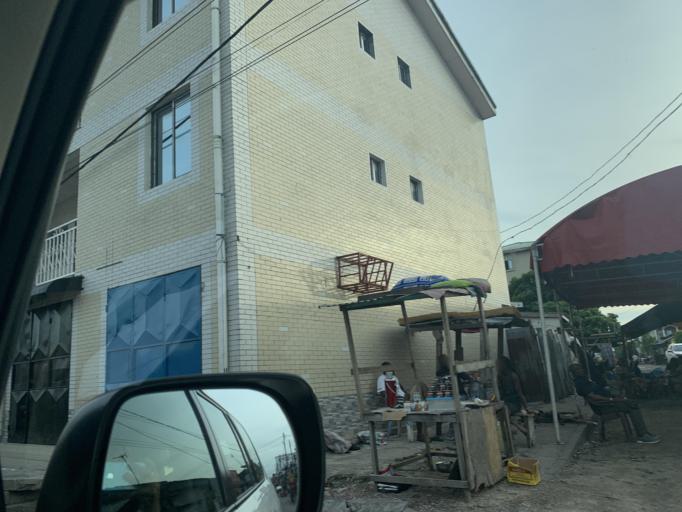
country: CG
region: Brazzaville
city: Brazzaville
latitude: -4.2502
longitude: 15.2848
